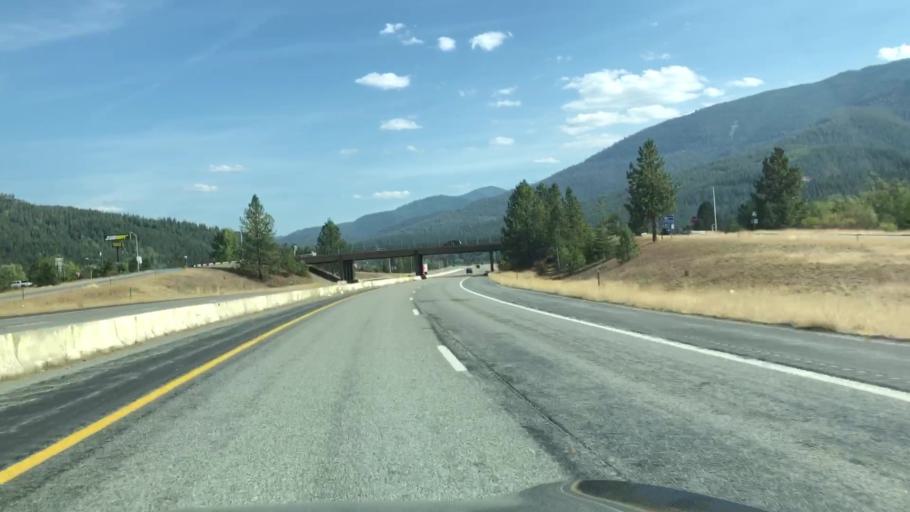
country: US
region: Idaho
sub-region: Shoshone County
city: Kellogg
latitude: 47.5470
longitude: -116.1351
